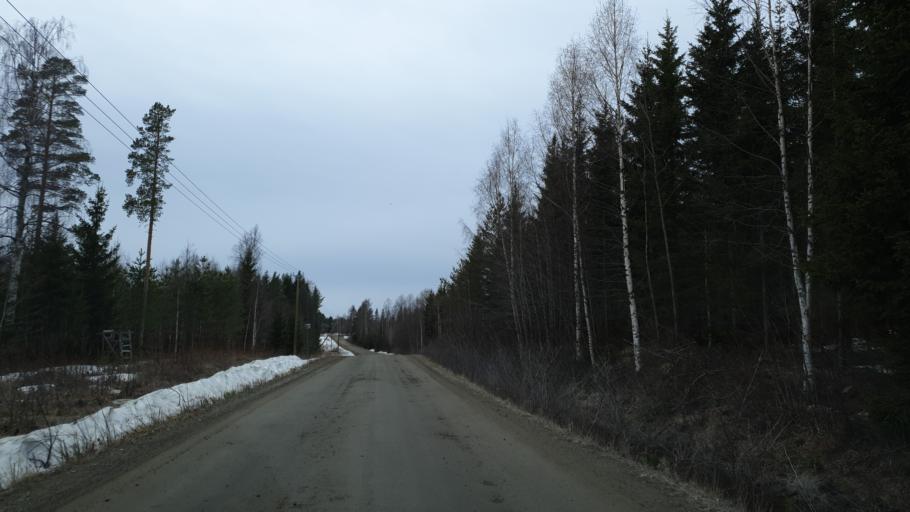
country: SE
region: Vaesterbotten
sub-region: Robertsfors Kommun
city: Robertsfors
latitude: 64.3919
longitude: 20.9791
